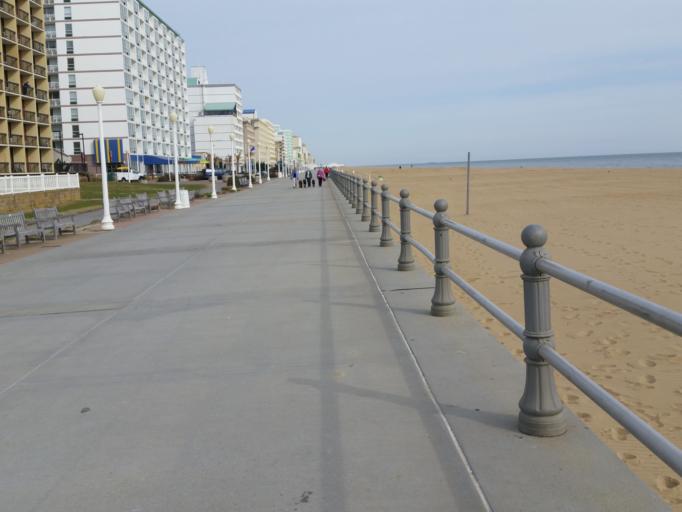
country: US
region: Virginia
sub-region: City of Virginia Beach
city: Virginia Beach
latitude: 36.8435
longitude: -75.9727
